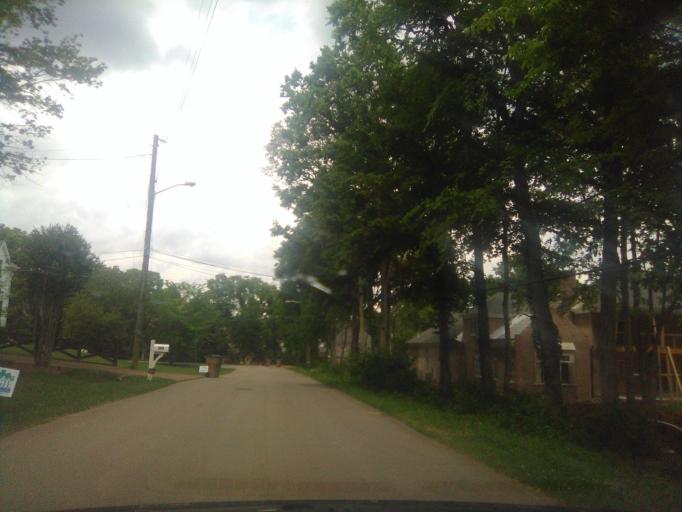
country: US
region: Tennessee
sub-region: Davidson County
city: Belle Meade
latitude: 36.0877
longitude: -86.8716
